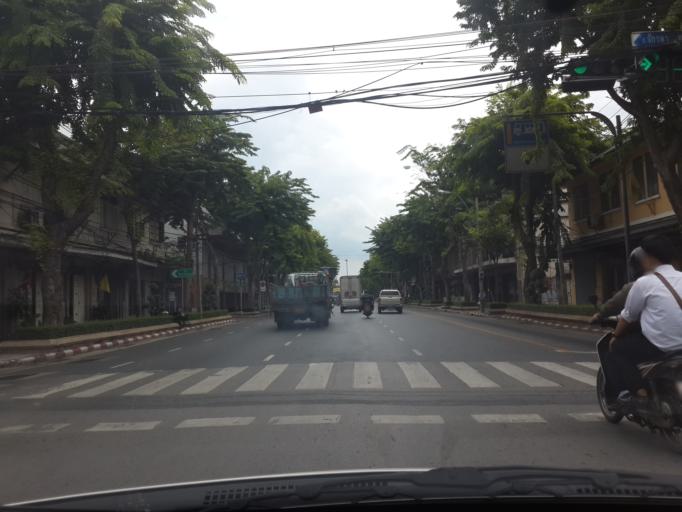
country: TH
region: Bangkok
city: Pom Prap Sattru Phai
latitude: 13.7565
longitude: 100.5096
